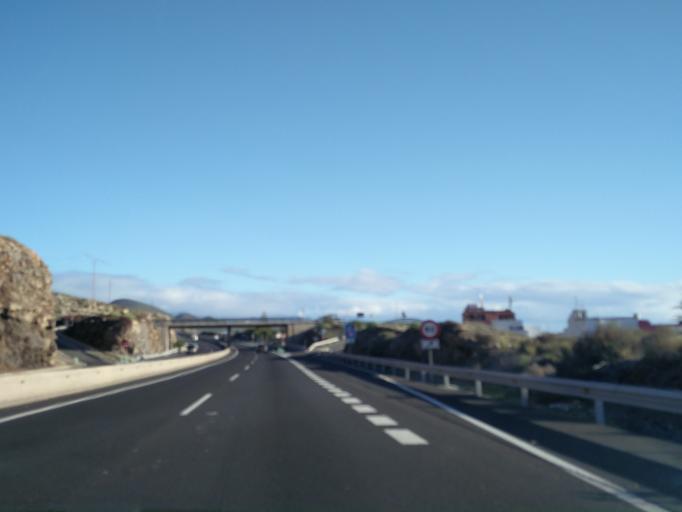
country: ES
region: Canary Islands
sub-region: Provincia de Santa Cruz de Tenerife
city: Guimar
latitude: 28.2705
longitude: -16.3868
